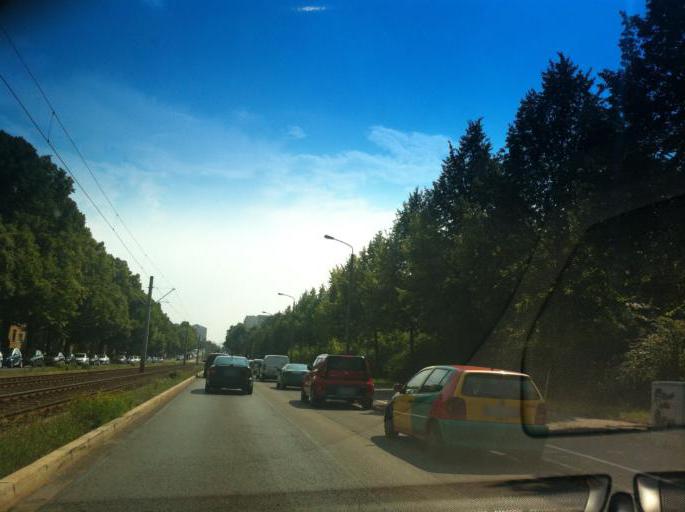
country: DE
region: Saxony
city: Leipzig
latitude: 51.3083
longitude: 12.3963
